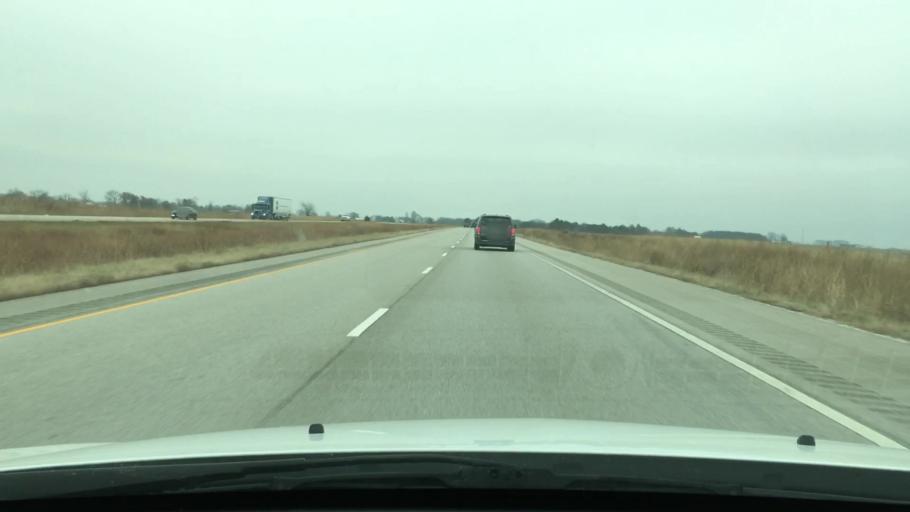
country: US
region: Illinois
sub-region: Sangamon County
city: New Berlin
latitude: 39.7378
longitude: -89.9790
